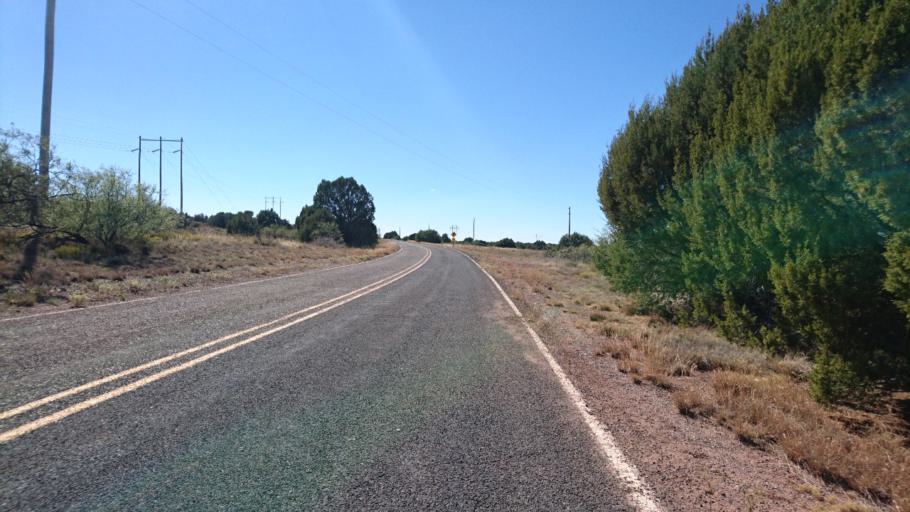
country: US
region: New Mexico
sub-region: Quay County
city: Tucumcari
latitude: 35.0672
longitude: -104.1740
